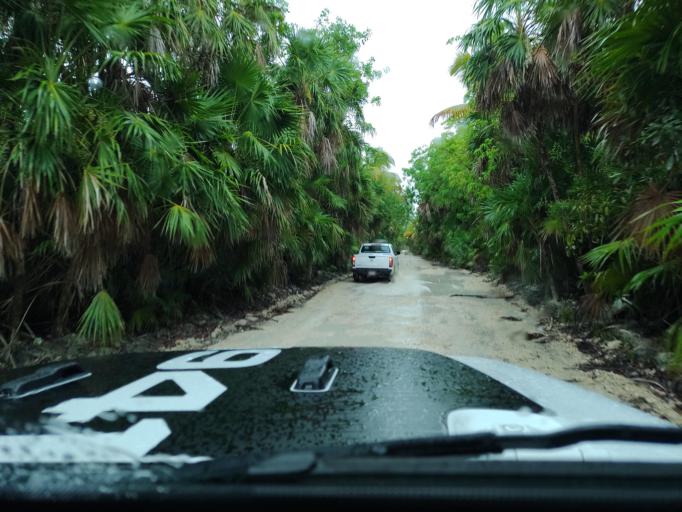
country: MX
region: Quintana Roo
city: Tulum
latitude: 19.9753
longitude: -87.4692
